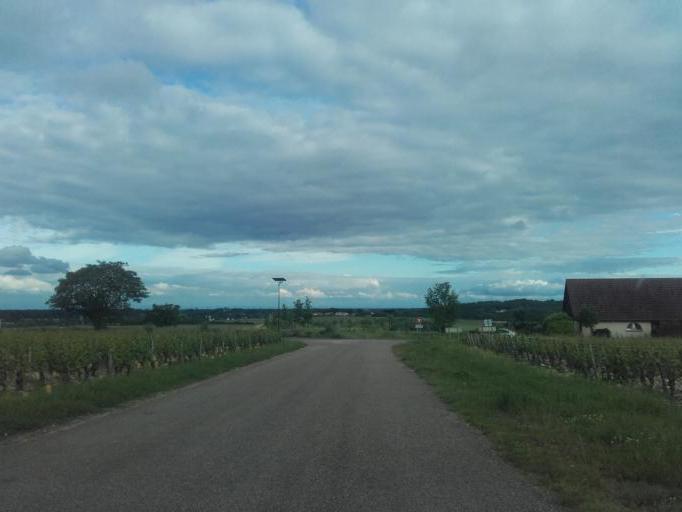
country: FR
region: Bourgogne
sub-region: Departement de Saone-et-Loire
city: Mellecey
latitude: 46.8240
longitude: 4.7282
